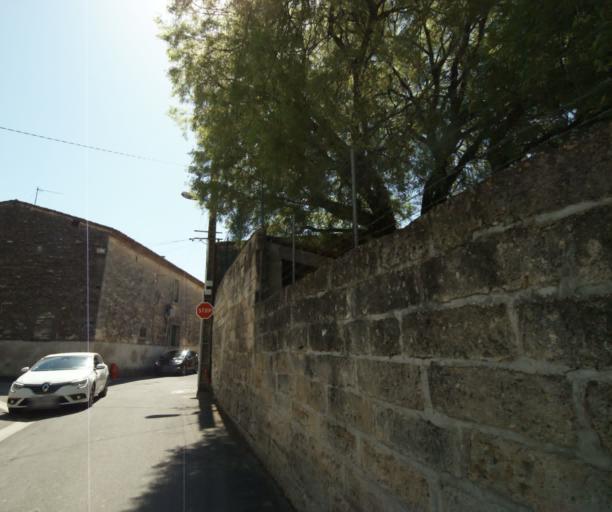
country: FR
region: Languedoc-Roussillon
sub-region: Departement de l'Herault
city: Sussargues
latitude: 43.7129
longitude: 4.0036
